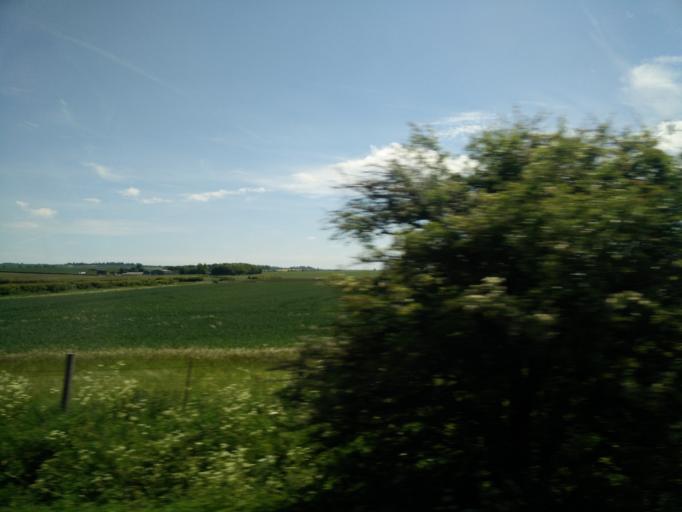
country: GB
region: England
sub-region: Hertfordshire
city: Baldock
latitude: 52.0113
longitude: -0.1348
